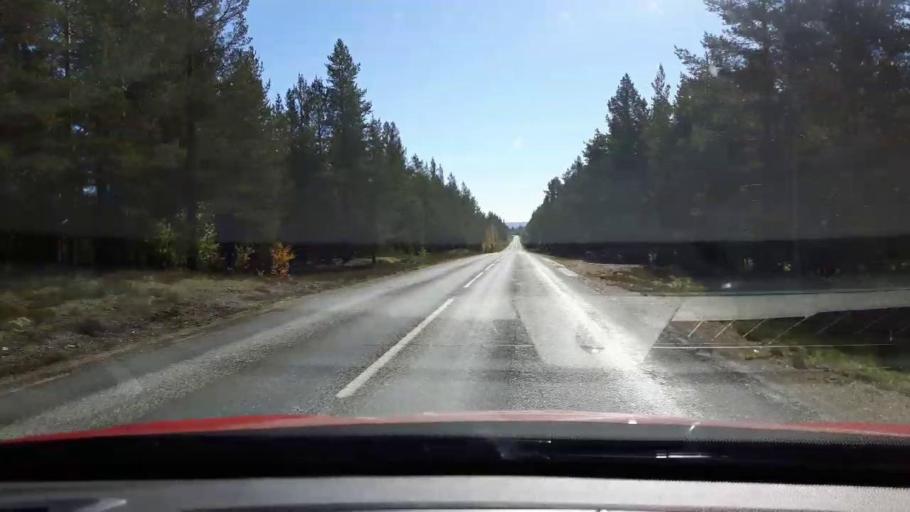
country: SE
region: Jaemtland
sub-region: Harjedalens Kommun
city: Sveg
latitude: 62.3745
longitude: 13.9780
